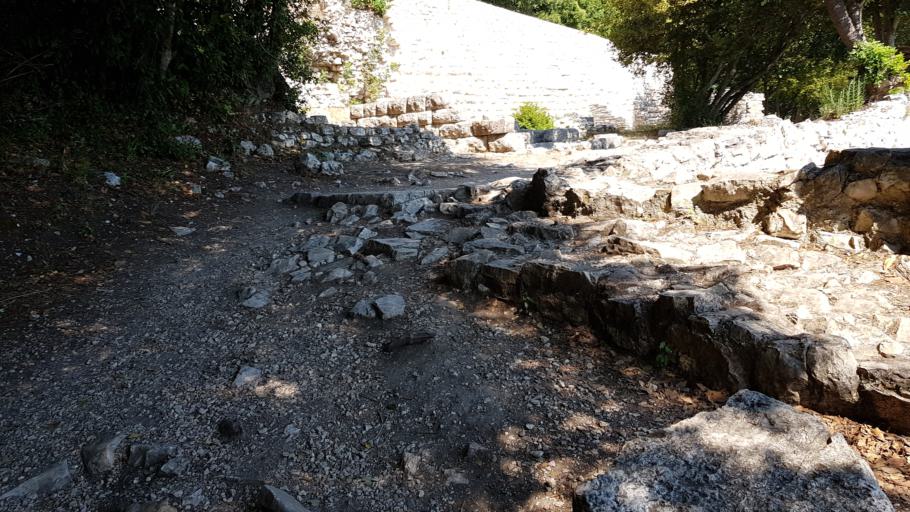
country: AL
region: Vlore
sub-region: Rrethi i Sarandes
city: Xarre
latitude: 39.7473
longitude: 20.0231
